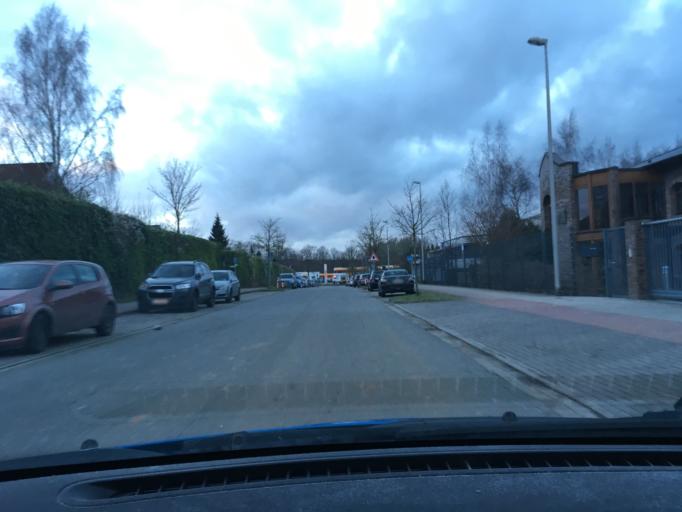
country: DE
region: Schleswig-Holstein
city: Rellingen
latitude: 53.6465
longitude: 9.8229
